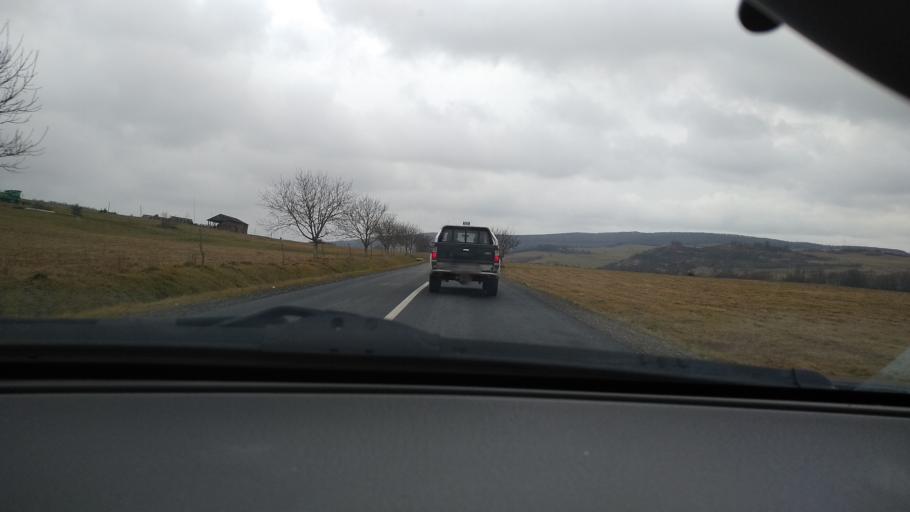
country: RO
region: Mures
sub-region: Comuna Bereni
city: Bereni
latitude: 46.5586
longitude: 24.8829
